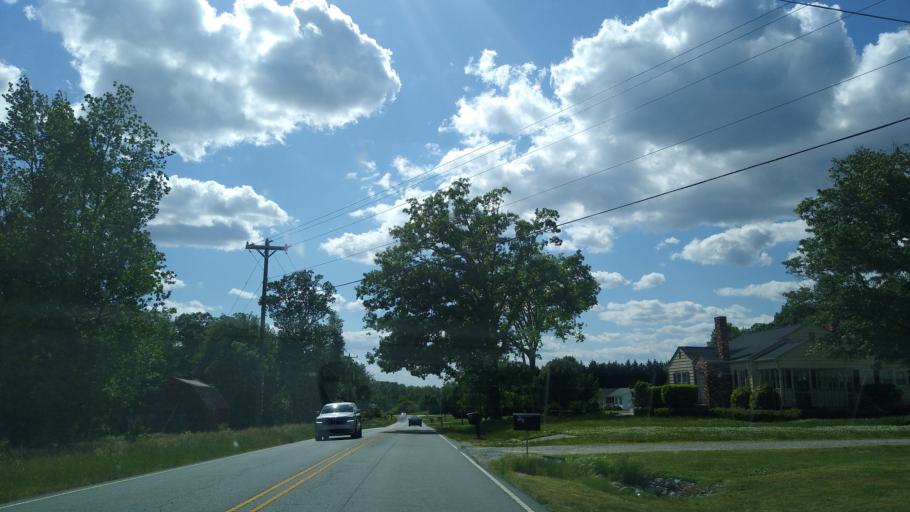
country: US
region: North Carolina
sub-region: Forsyth County
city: Kernersville
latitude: 36.1015
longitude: -80.0939
